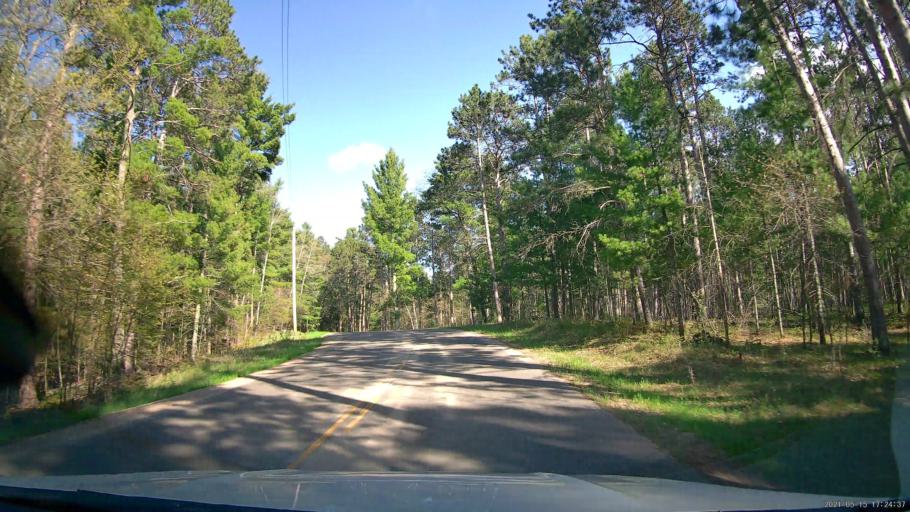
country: US
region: Minnesota
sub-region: Hubbard County
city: Park Rapids
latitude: 46.9924
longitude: -94.9571
